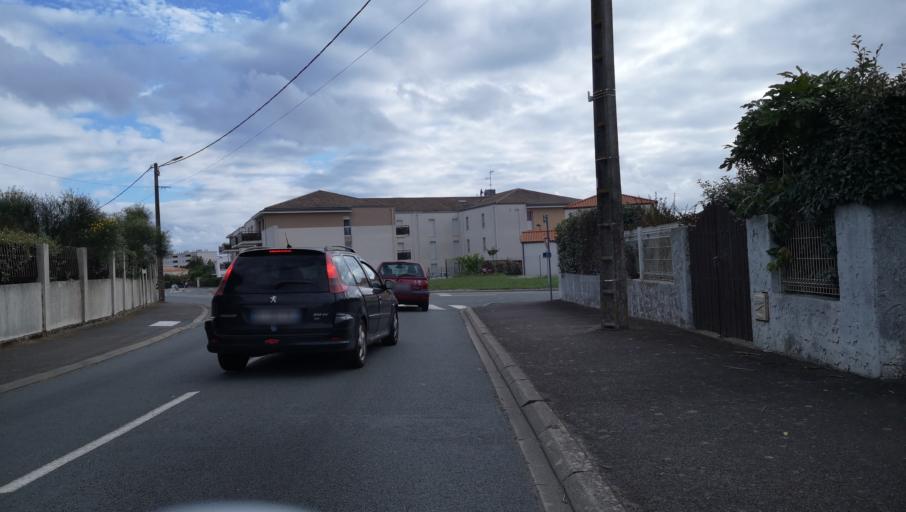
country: FR
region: Pays de la Loire
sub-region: Departement de la Vendee
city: Les Sables-d'Olonne
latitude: 46.5090
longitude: -1.7817
